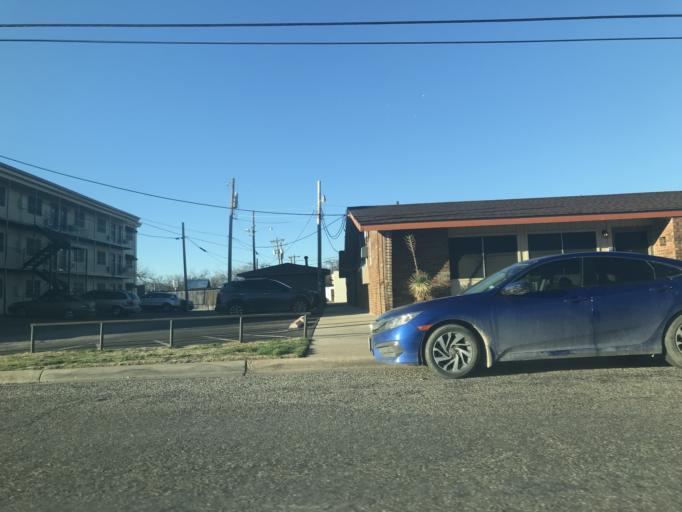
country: US
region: Texas
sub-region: Tom Green County
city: San Angelo
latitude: 31.4420
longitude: -100.4615
